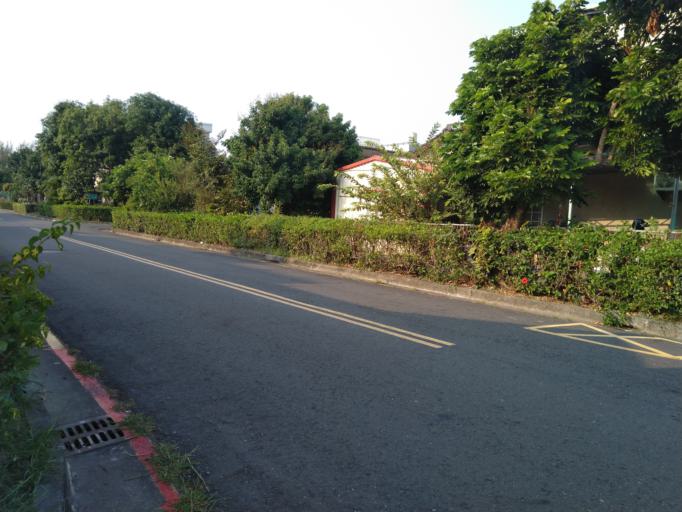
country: TW
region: Kaohsiung
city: Kaohsiung
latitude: 22.7128
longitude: 120.3049
